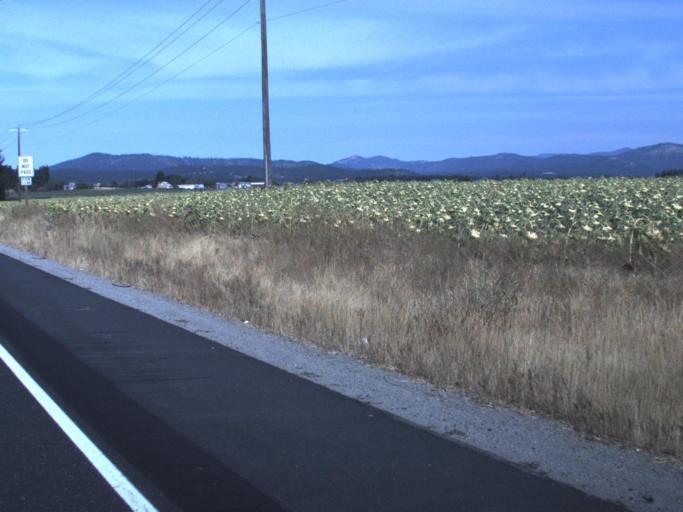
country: US
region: Washington
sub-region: Spokane County
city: Deer Park
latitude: 47.9650
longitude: -117.5036
